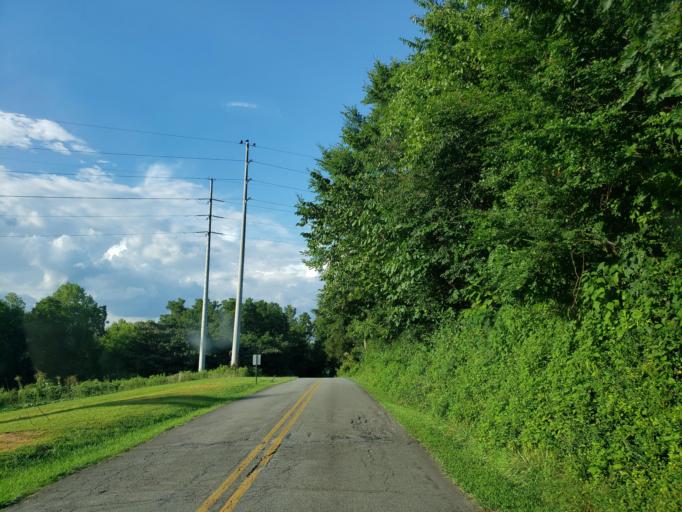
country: US
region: Georgia
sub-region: Bartow County
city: Rydal
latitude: 34.2875
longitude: -84.7438
